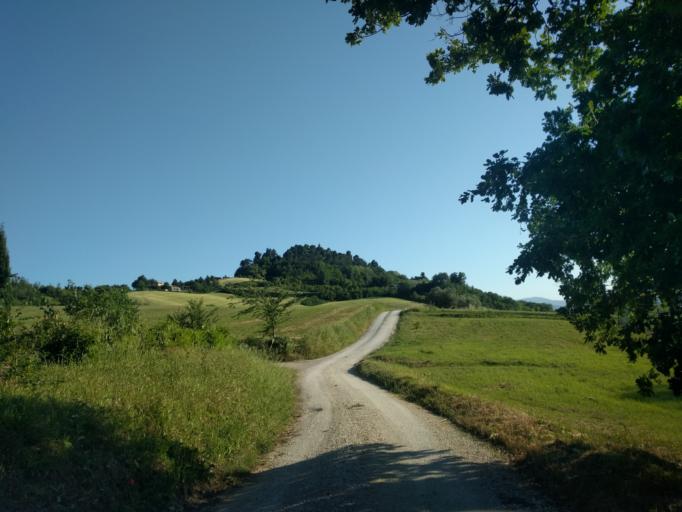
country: IT
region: The Marches
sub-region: Provincia di Pesaro e Urbino
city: Montemaggiore al Metauro
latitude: 43.7436
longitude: 12.9518
